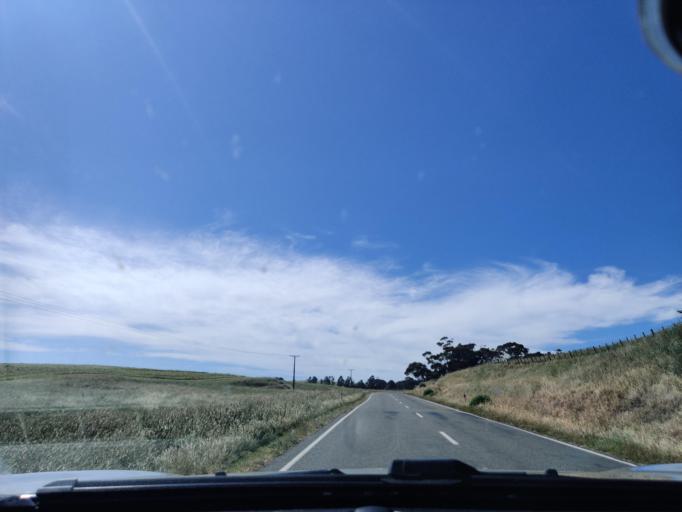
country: NZ
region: Wellington
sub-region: South Wairarapa District
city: Waipawa
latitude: -41.2012
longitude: 175.3629
